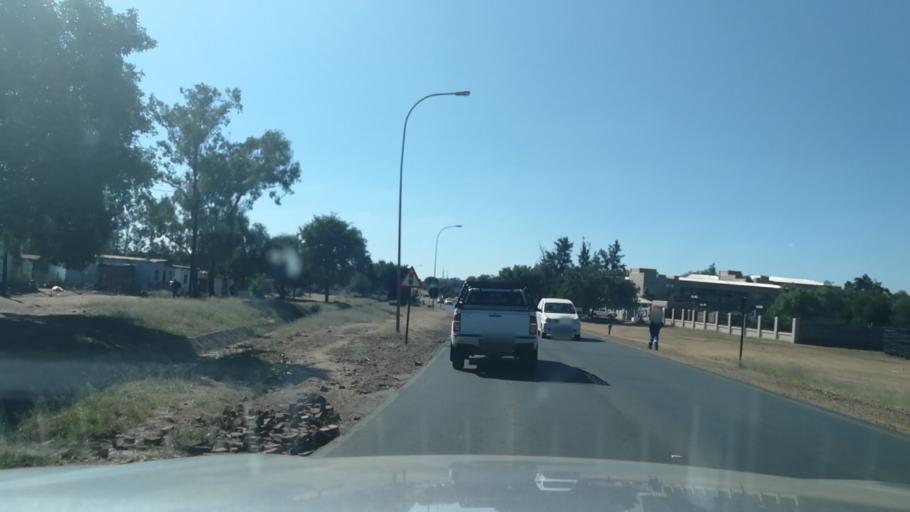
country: BW
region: South East
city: Gaborone
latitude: -24.6850
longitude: 25.9054
